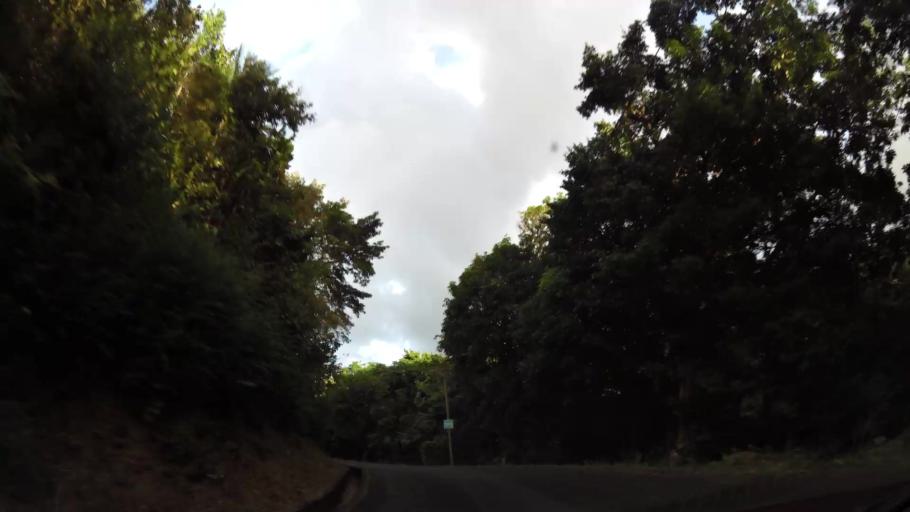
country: DM
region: Saint John
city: Portsmouth
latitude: 15.5738
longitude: -61.4384
